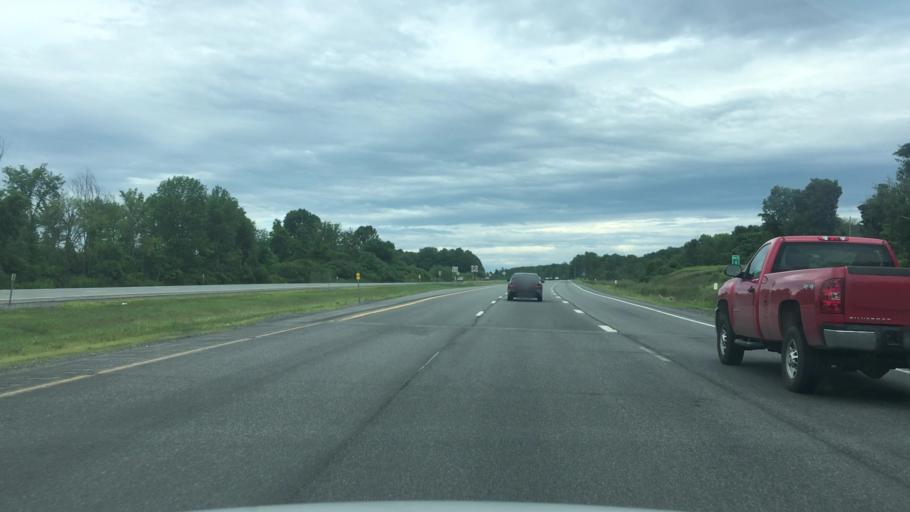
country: US
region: New York
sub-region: Schoharie County
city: Schoharie
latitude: 42.7146
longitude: -74.2723
